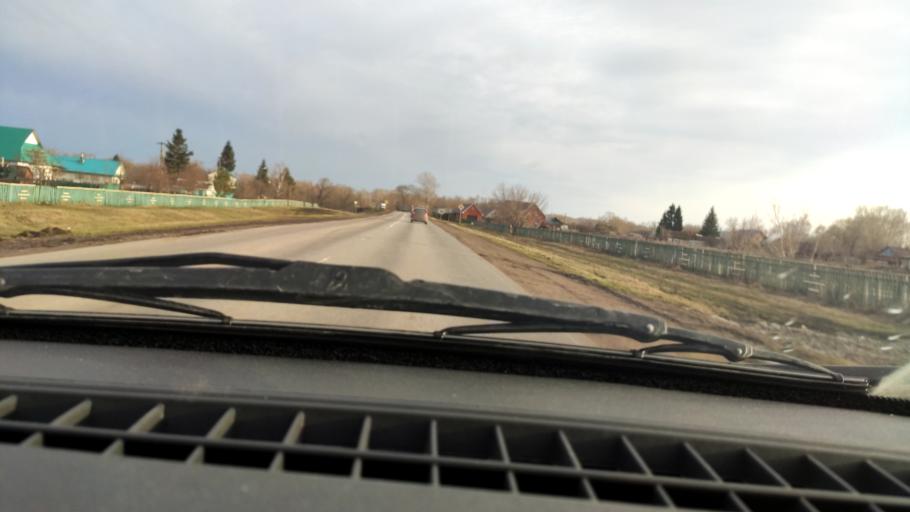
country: RU
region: Bashkortostan
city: Davlekanovo
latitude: 54.3692
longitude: 55.1953
